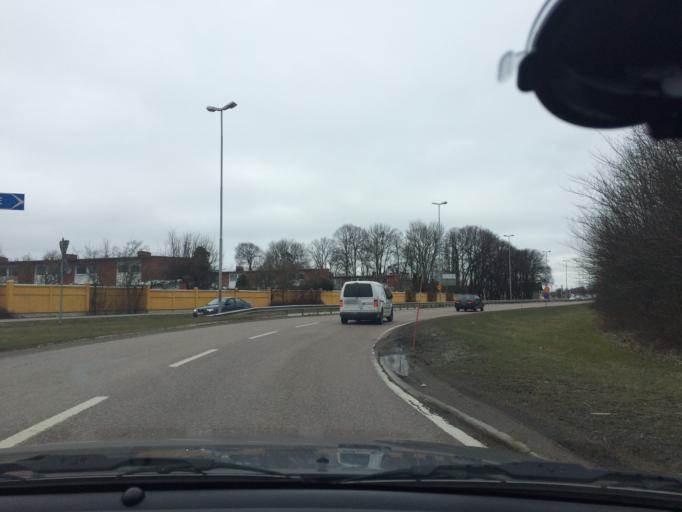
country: SE
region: Vaestmanland
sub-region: Vasteras
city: Vasteras
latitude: 59.6317
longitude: 16.5562
